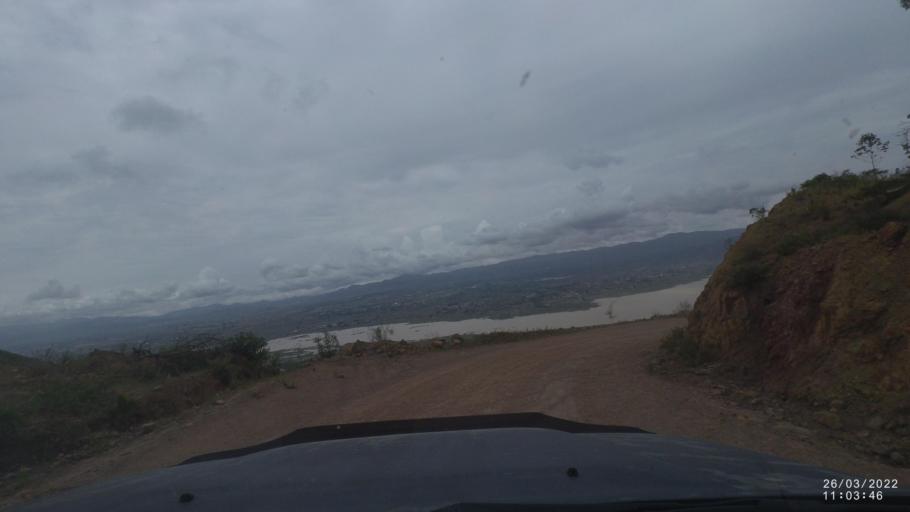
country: BO
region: Cochabamba
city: Tarata
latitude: -17.5288
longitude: -66.0243
